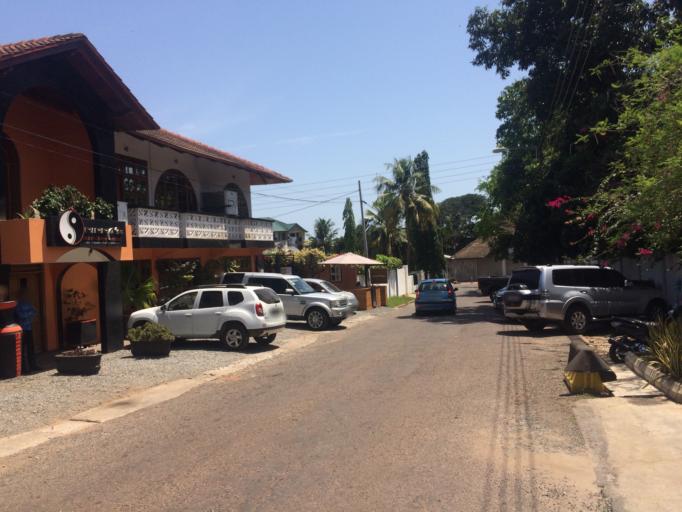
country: GH
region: Greater Accra
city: Accra
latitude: 5.5656
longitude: -0.1889
